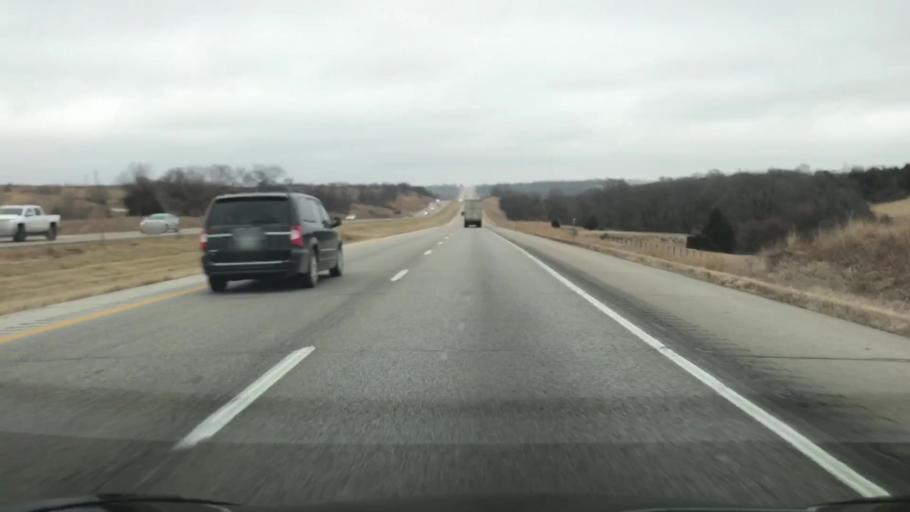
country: US
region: Iowa
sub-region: Madison County
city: Earlham
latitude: 41.5178
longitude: -94.1691
